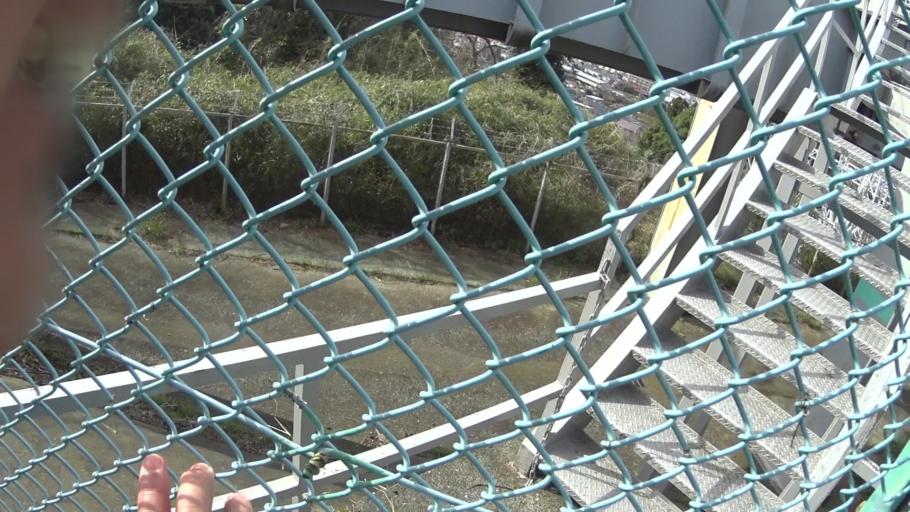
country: JP
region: Kanagawa
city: Kamakura
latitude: 35.3256
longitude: 139.5139
